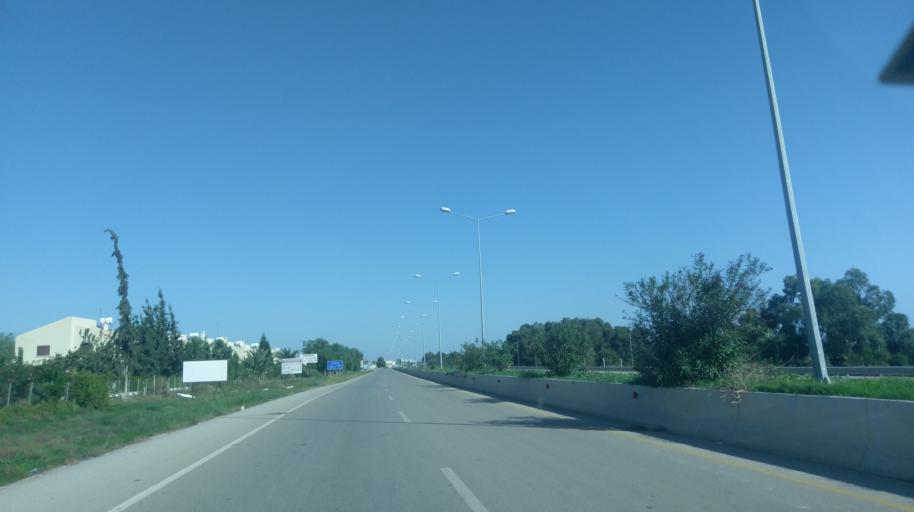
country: CY
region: Ammochostos
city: Trikomo
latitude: 35.2745
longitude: 33.9171
